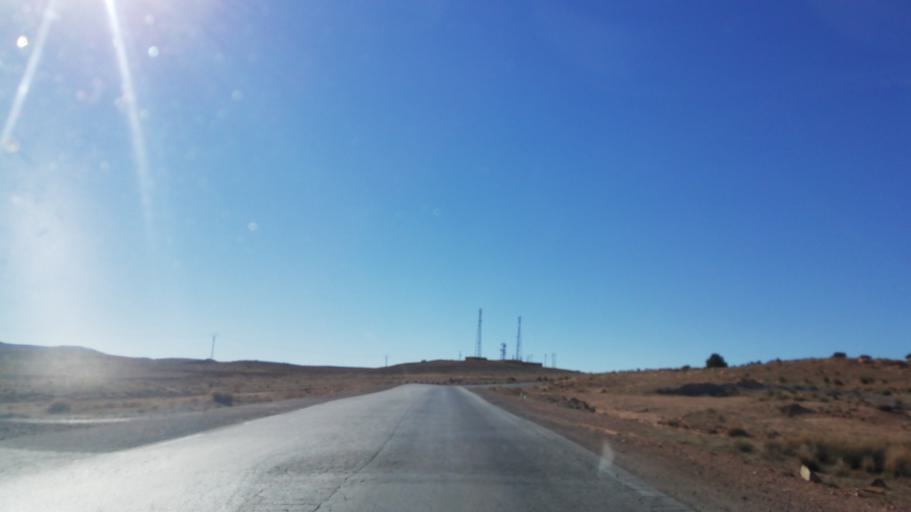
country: DZ
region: El Bayadh
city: El Bayadh
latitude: 33.6637
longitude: 1.4287
